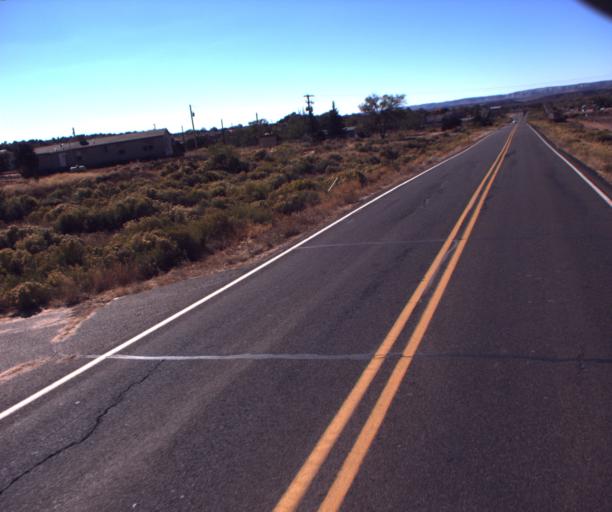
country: US
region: Arizona
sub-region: Apache County
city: Ganado
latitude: 35.7094
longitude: -109.5349
